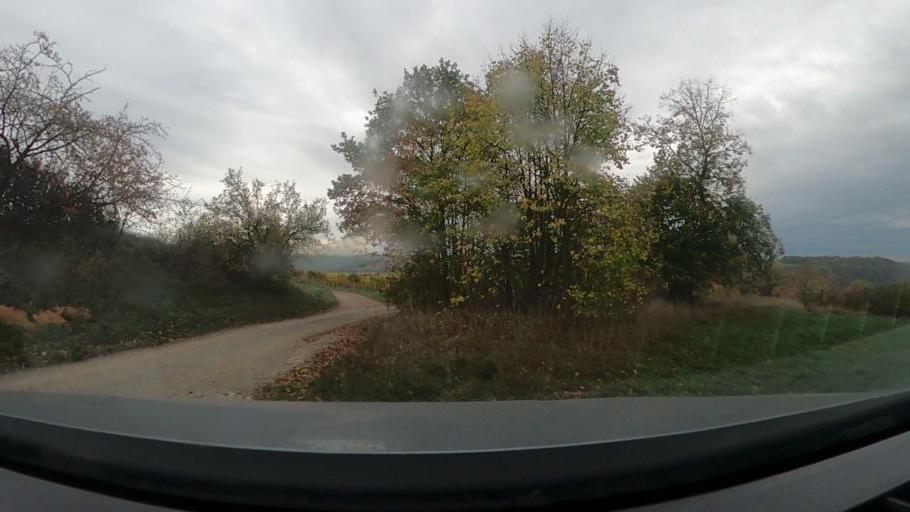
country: DE
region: Thuringia
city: Grossheringen
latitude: 51.1090
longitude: 11.6483
